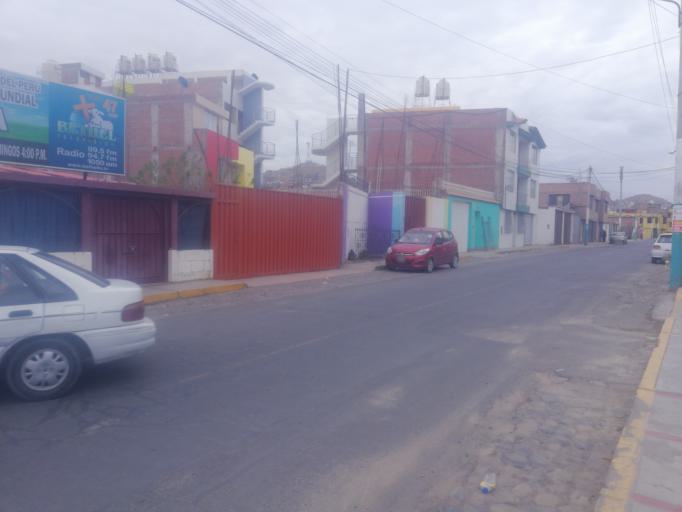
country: PE
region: Arequipa
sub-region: Provincia de Arequipa
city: Tiabaya
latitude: -16.4476
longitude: -71.5890
